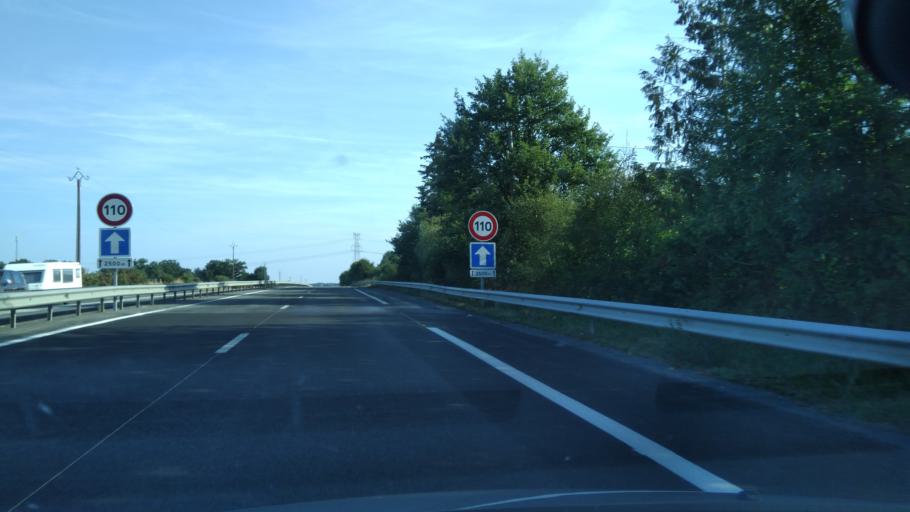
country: FR
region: Pays de la Loire
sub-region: Departement de la Mayenne
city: Entrammes
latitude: 47.9384
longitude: -0.6965
